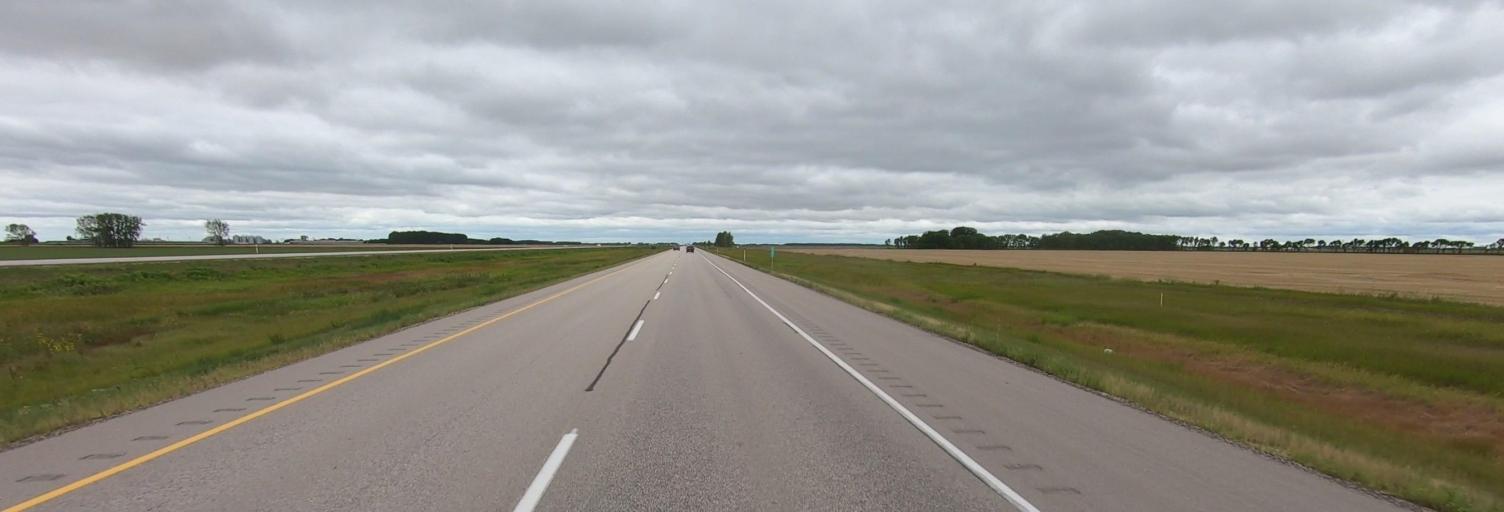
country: CA
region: Manitoba
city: Headingley
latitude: 49.9185
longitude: -97.8190
